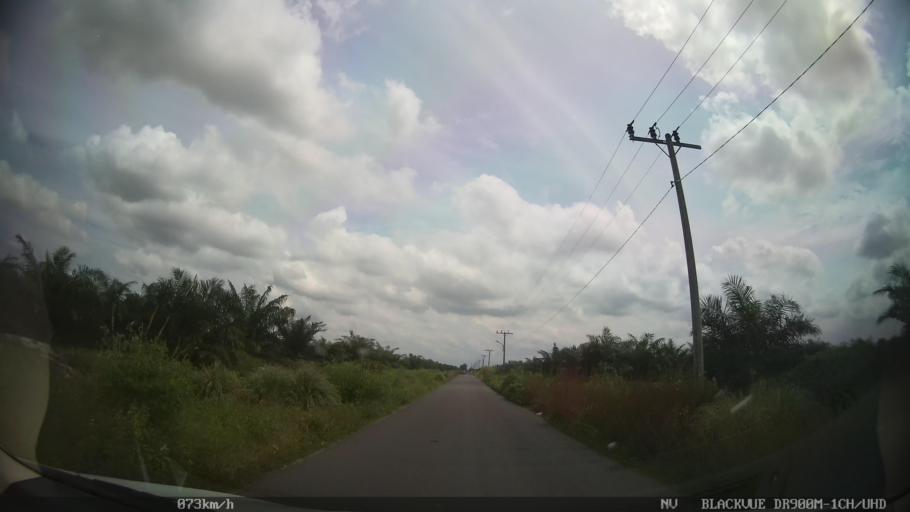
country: ID
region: North Sumatra
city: Percut
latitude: 3.5848
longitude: 98.8409
